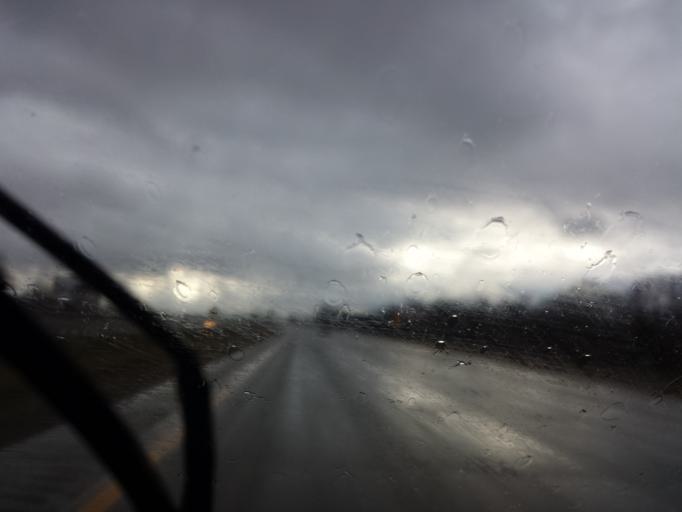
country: US
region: Michigan
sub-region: Genesee County
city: Swartz Creek
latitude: 42.9772
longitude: -83.7570
